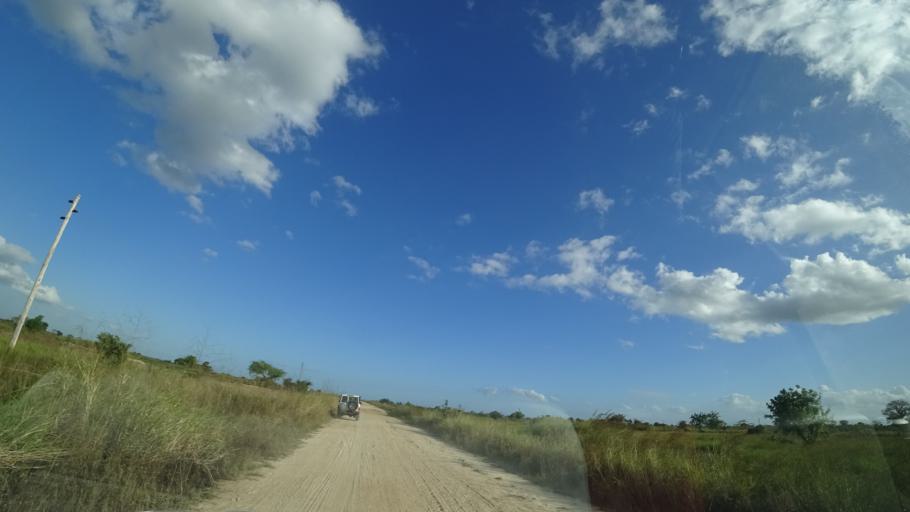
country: MZ
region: Sofala
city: Dondo
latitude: -19.4434
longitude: 34.5620
